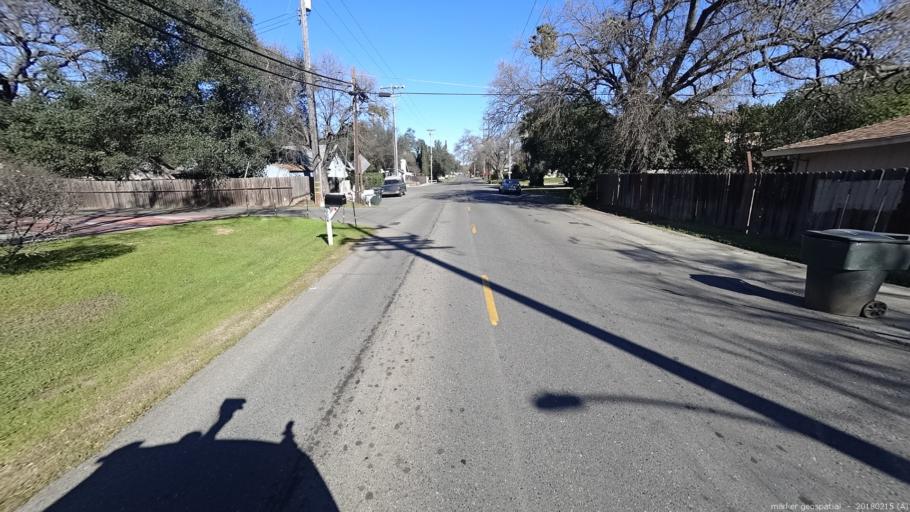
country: US
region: California
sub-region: Sacramento County
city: Foothill Farms
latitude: 38.6642
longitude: -121.3321
